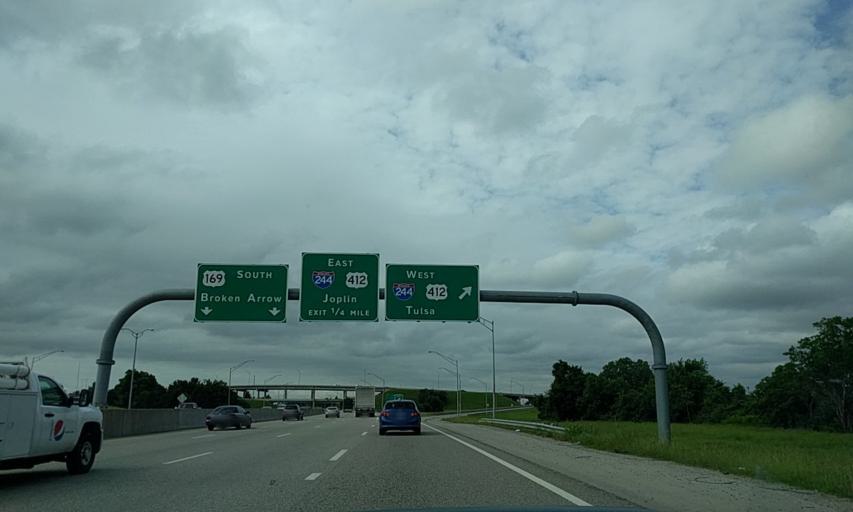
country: US
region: Oklahoma
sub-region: Tulsa County
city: Owasso
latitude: 36.1697
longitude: -95.8605
